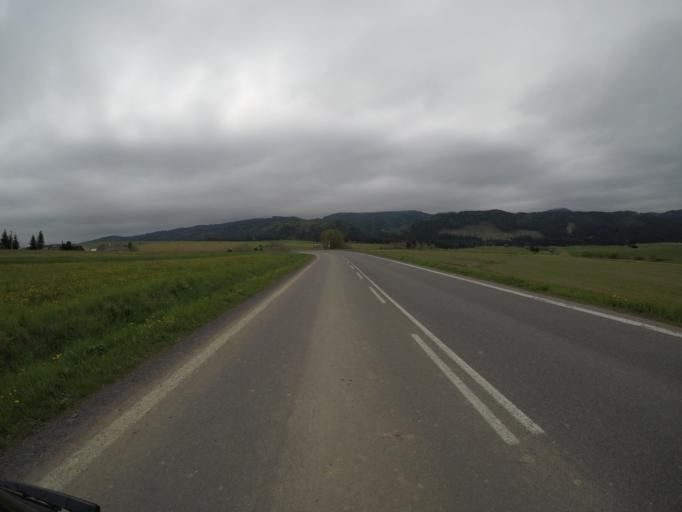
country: SK
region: Zilinsky
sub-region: Okres Liptovsky Mikulas
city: Hybe
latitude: 49.0562
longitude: 19.8732
